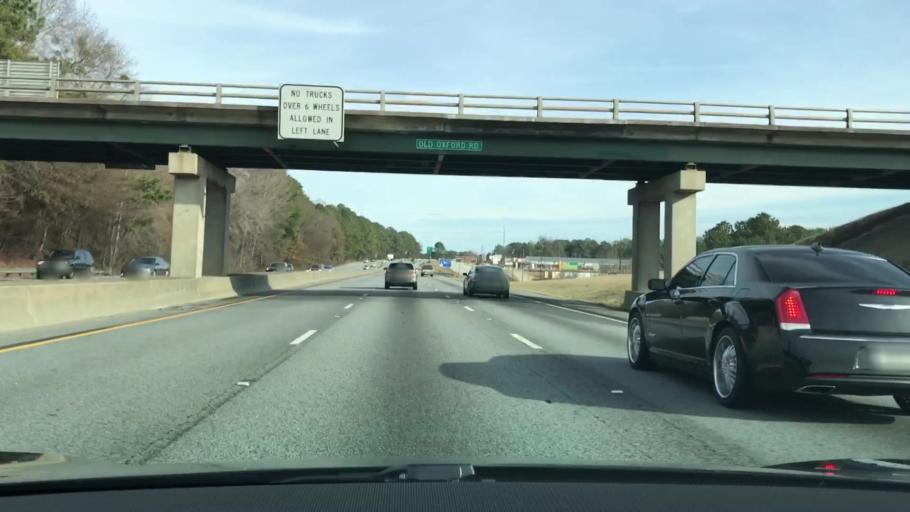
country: US
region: Georgia
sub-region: Newton County
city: Oxford
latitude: 33.6132
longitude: -83.9013
